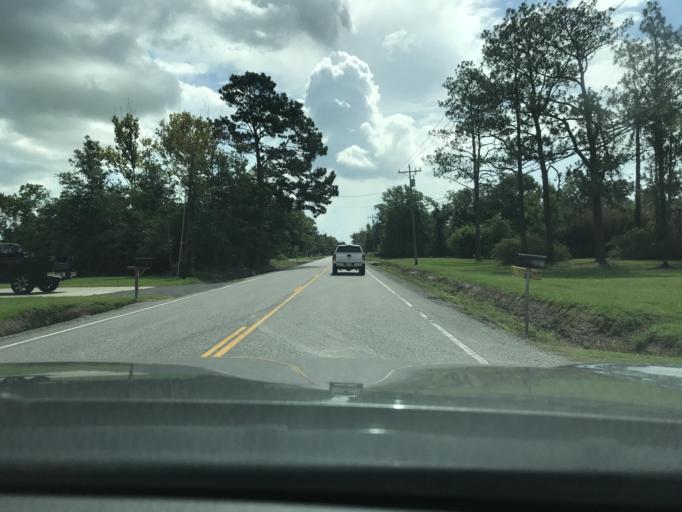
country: US
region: Louisiana
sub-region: Calcasieu Parish
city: Moss Bluff
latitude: 30.3447
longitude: -93.2174
